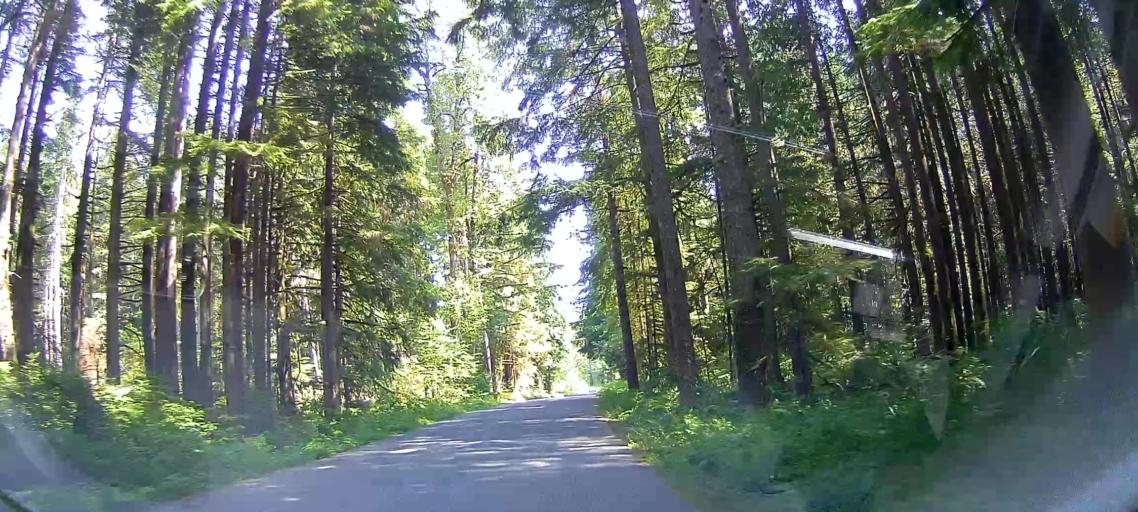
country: US
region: Washington
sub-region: Snohomish County
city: Arlington Heights
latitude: 48.3373
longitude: -122.0256
